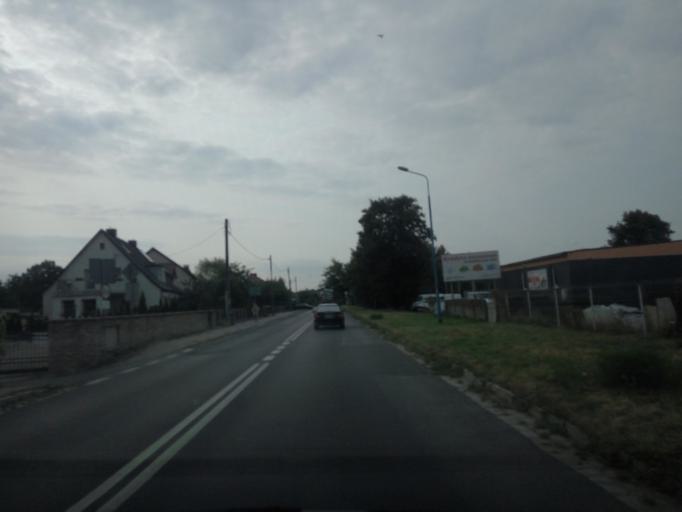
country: PL
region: Lower Silesian Voivodeship
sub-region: Powiat strzelinski
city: Strzelin
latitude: 50.7907
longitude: 17.0663
